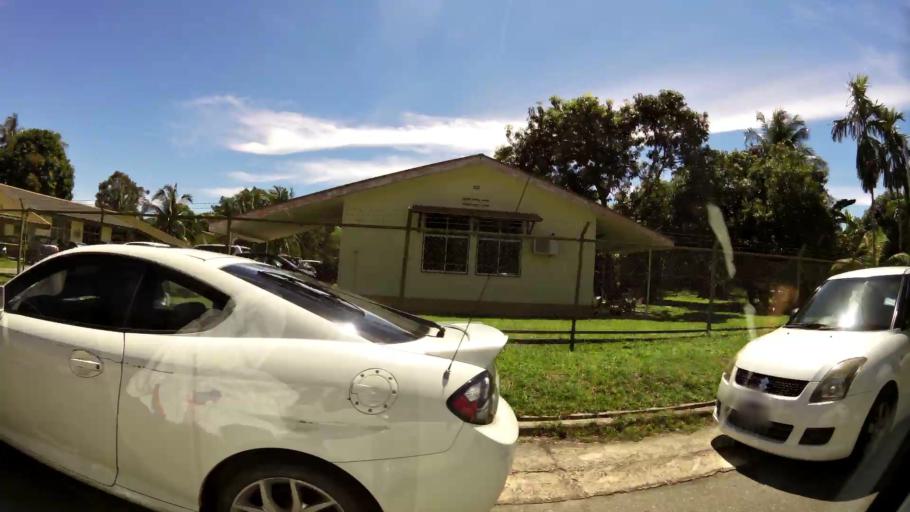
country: BN
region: Brunei and Muara
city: Bandar Seri Begawan
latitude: 5.0350
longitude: 115.0787
